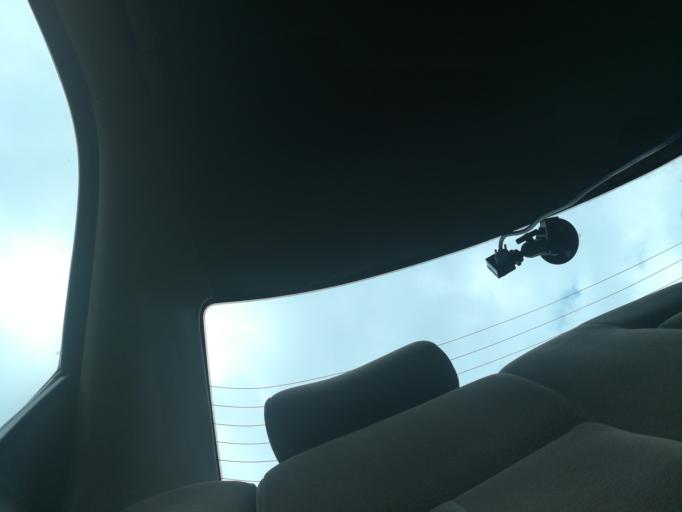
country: NG
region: Lagos
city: Ikorodu
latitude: 6.6571
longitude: 3.5834
